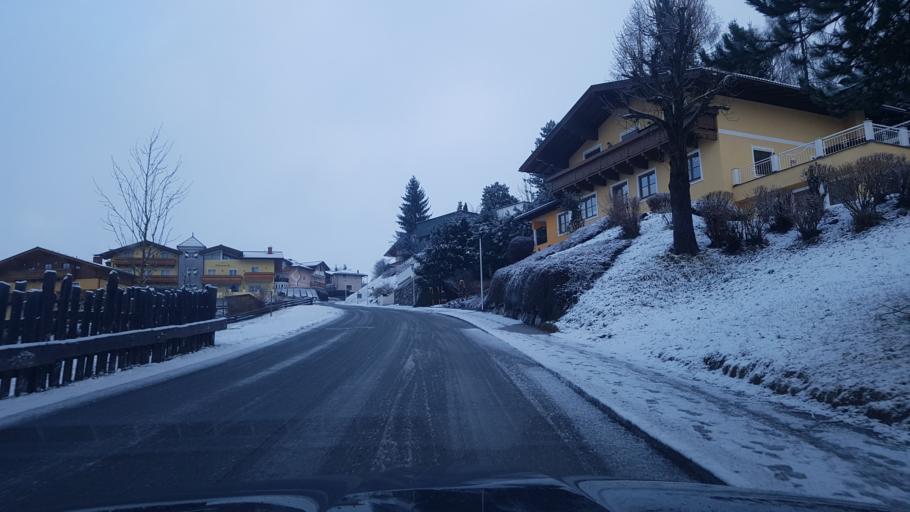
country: AT
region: Salzburg
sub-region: Politischer Bezirk Sankt Johann im Pongau
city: Sankt Johann im Pongau
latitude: 47.3259
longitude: 13.2000
